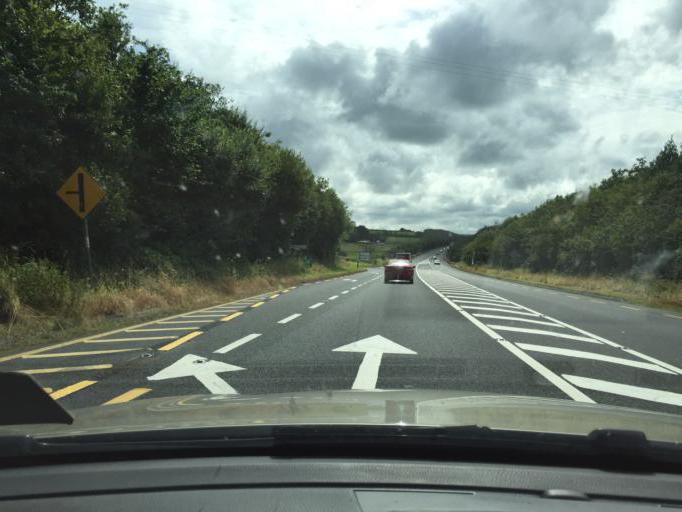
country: IE
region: Munster
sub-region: Waterford
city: Portlaw
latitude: 52.2009
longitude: -7.4130
